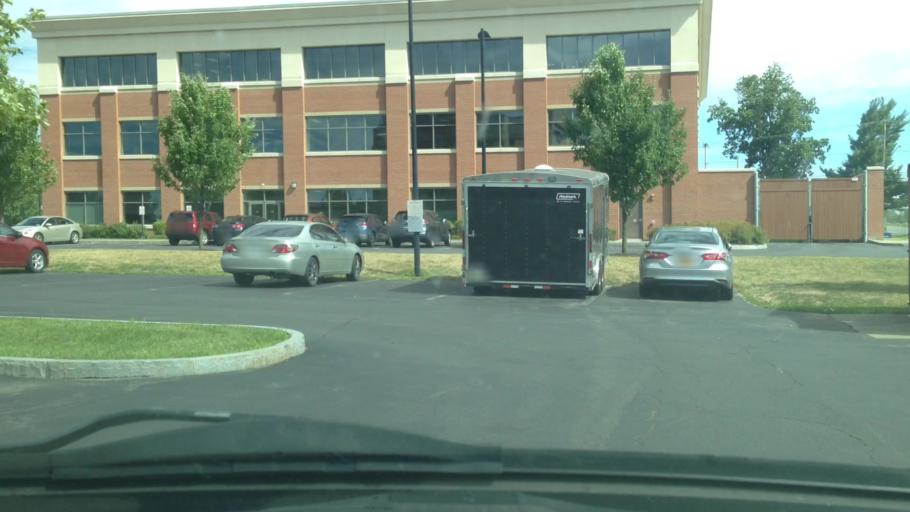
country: US
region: New York
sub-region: Onondaga County
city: East Syracuse
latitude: 43.0893
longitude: -76.0791
